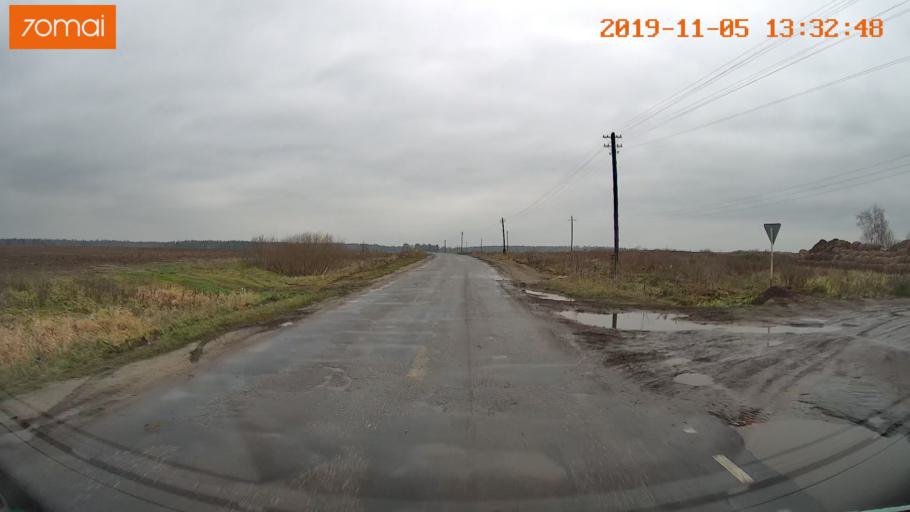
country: RU
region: Ivanovo
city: Shuya
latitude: 56.8864
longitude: 41.3966
